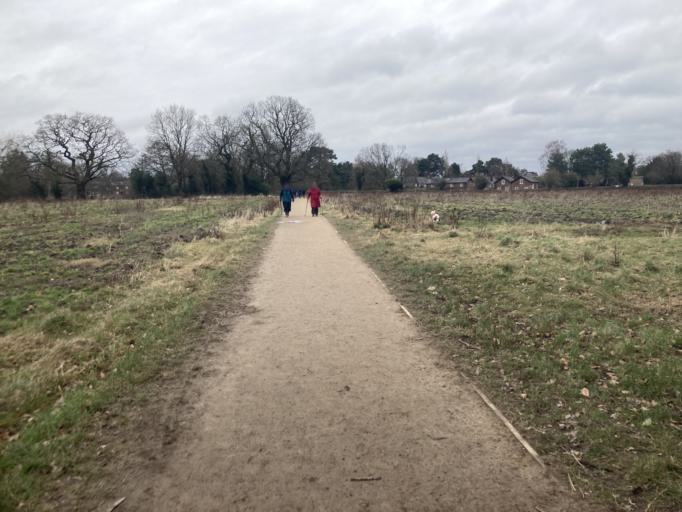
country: GB
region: England
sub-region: Cheshire East
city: Wilmslow
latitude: 53.3460
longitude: -2.2478
